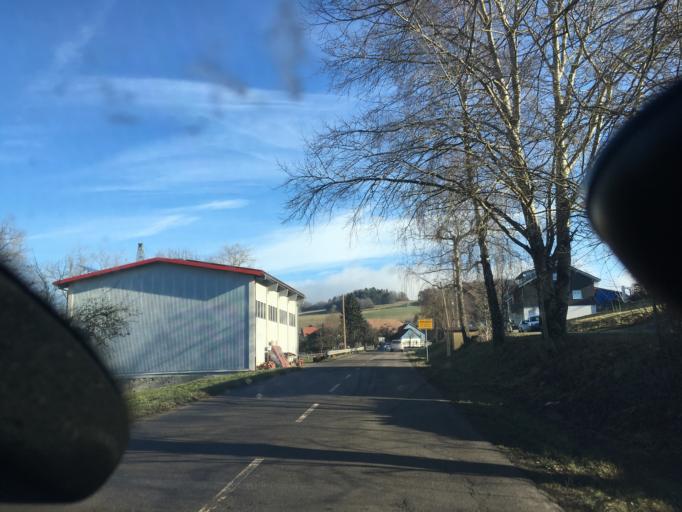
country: DE
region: Baden-Wuerttemberg
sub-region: Freiburg Region
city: Gorwihl
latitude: 47.6447
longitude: 8.1309
